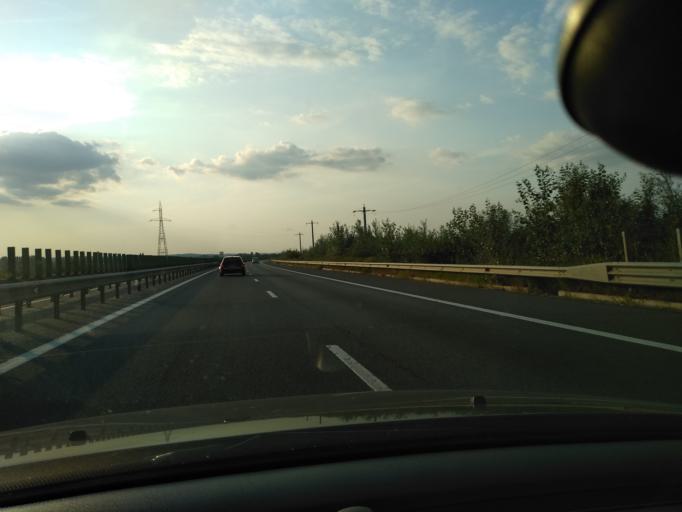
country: RO
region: Arges
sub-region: Comuna Maracineni
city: Maracineni
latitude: 44.8786
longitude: 24.8664
